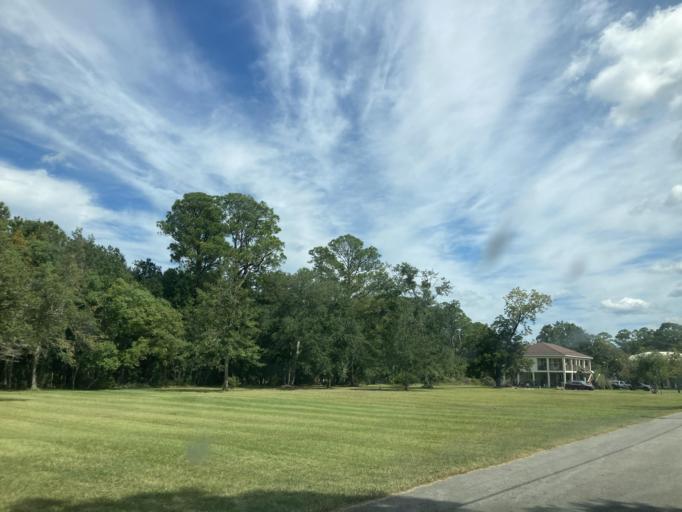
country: US
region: Mississippi
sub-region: Jackson County
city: Saint Martin
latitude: 30.4284
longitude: -88.8770
